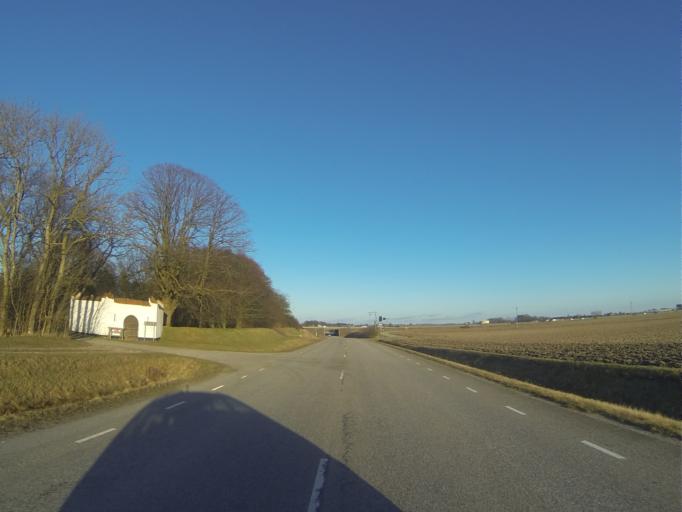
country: SE
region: Skane
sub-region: Malmo
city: Tygelsjo
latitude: 55.5431
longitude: 13.0003
